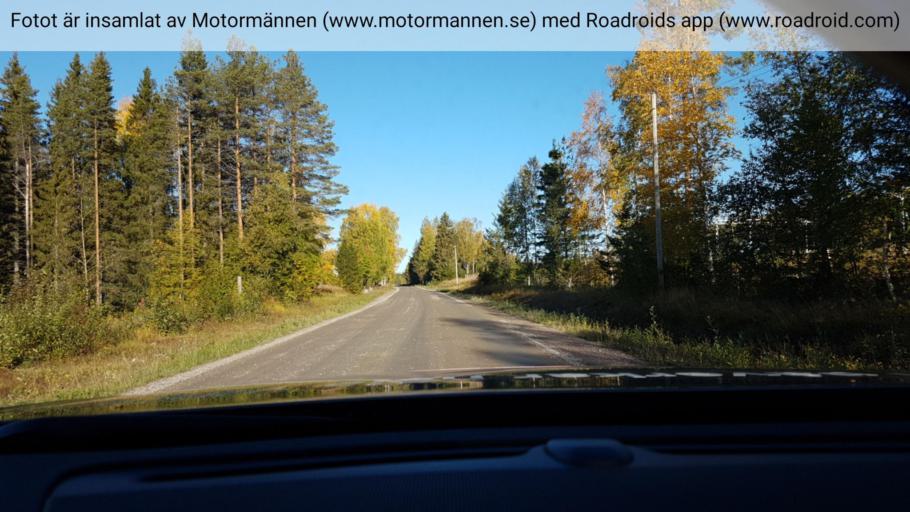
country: SE
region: Norrbotten
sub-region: Alvsbyns Kommun
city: AElvsbyn
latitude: 66.1940
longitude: 21.1921
